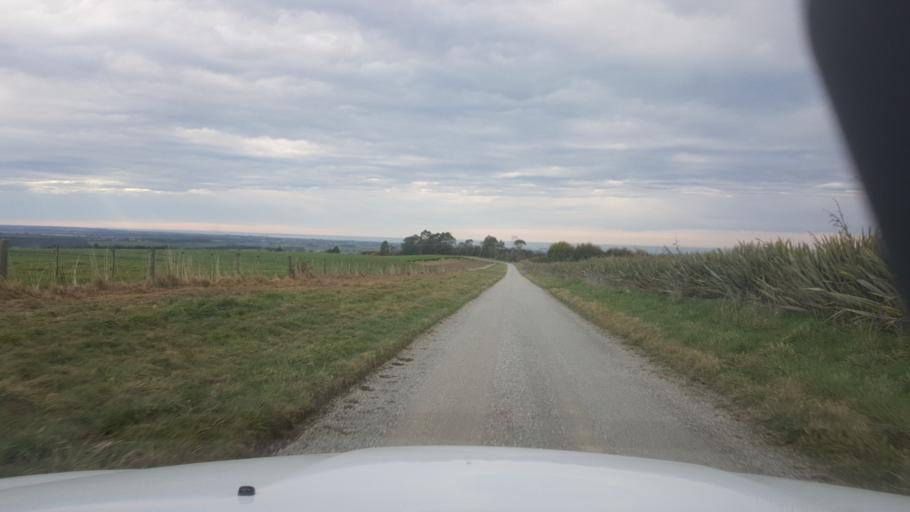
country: NZ
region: Canterbury
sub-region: Timaru District
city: Pleasant Point
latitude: -44.3456
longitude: 171.1265
